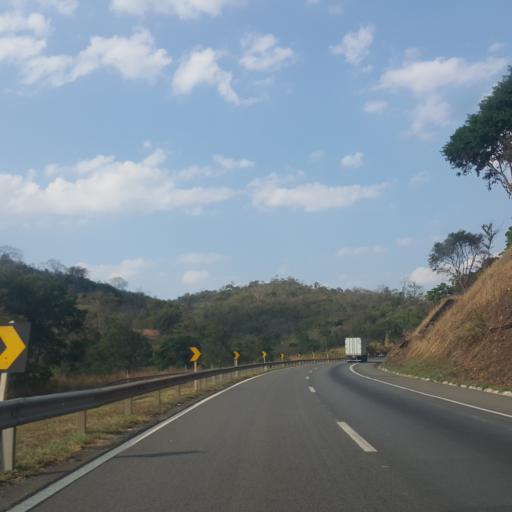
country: BR
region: Goias
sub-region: Abadiania
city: Abadiania
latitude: -16.1106
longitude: -48.5848
